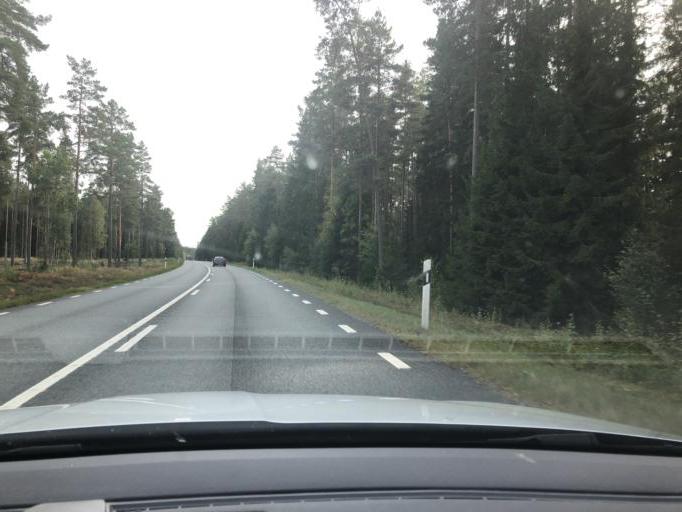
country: SE
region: Joenkoeping
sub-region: Eksjo Kommun
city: Eksjoe
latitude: 57.5878
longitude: 14.9683
